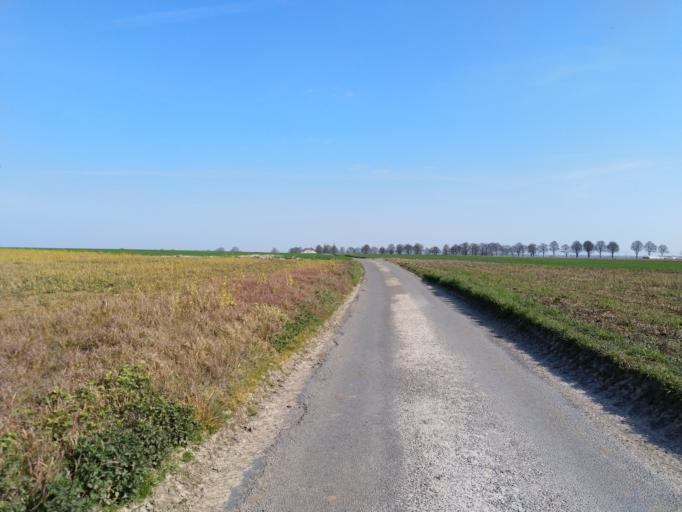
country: BE
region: Wallonia
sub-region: Province du Hainaut
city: Lens
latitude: 50.5610
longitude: 3.8825
